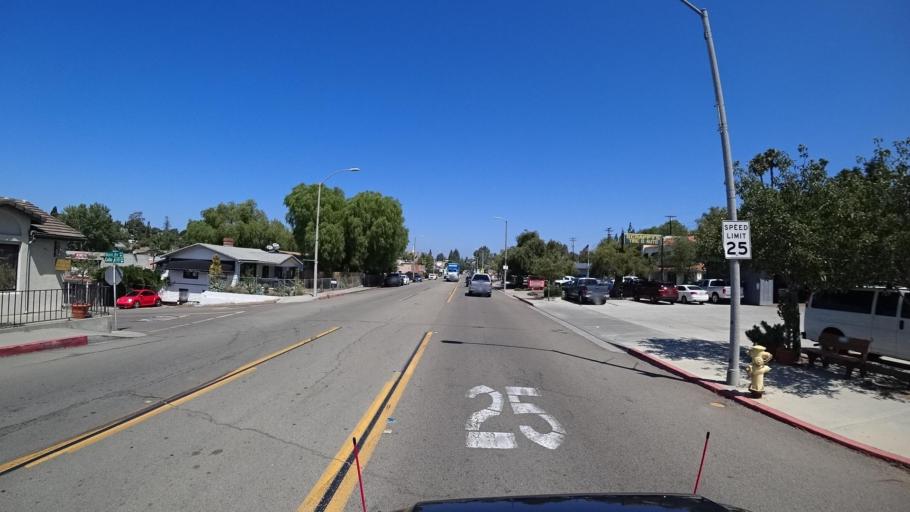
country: US
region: California
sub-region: San Diego County
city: Fallbrook
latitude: 33.3792
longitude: -117.2514
